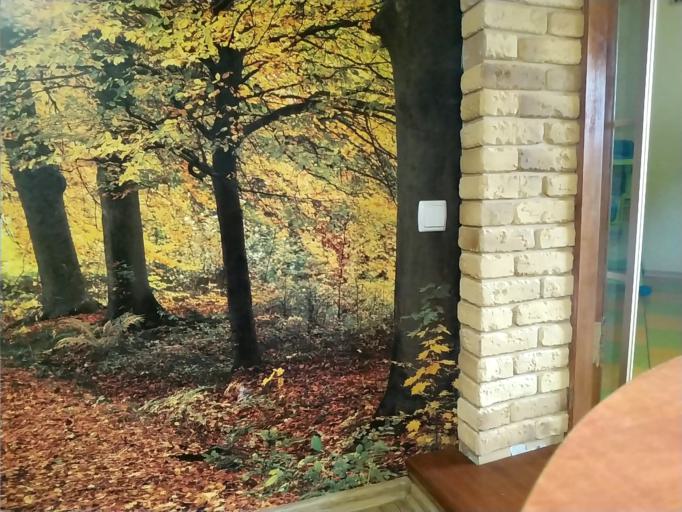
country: RU
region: Smolensk
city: Dorogobuzh
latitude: 54.8715
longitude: 33.3115
